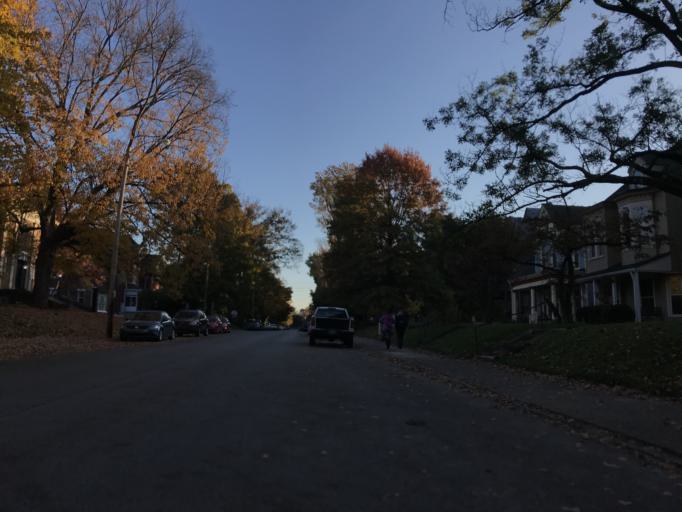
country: US
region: Kentucky
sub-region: Jefferson County
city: Audubon Park
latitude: 38.2372
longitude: -85.7274
